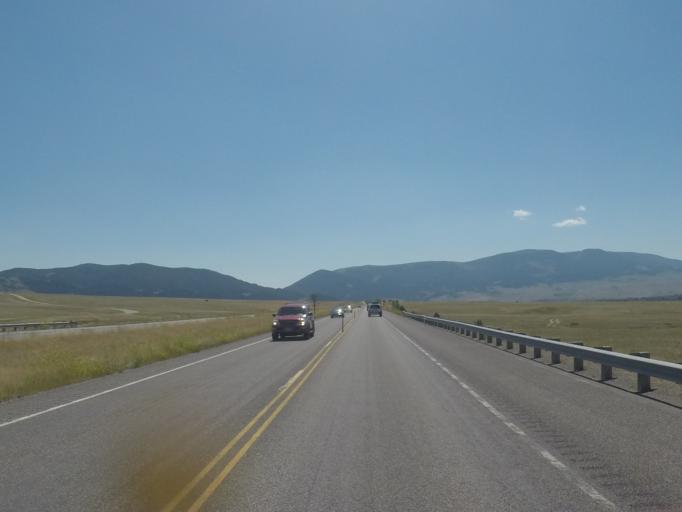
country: US
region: Montana
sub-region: Park County
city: Livingston
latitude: 45.6649
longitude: -110.5272
